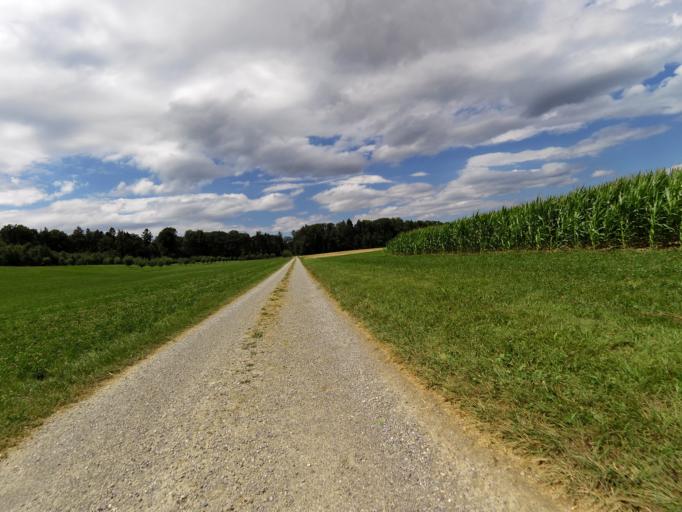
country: CH
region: Thurgau
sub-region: Kreuzlingen District
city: Ermatingen
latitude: 47.6512
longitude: 9.0834
